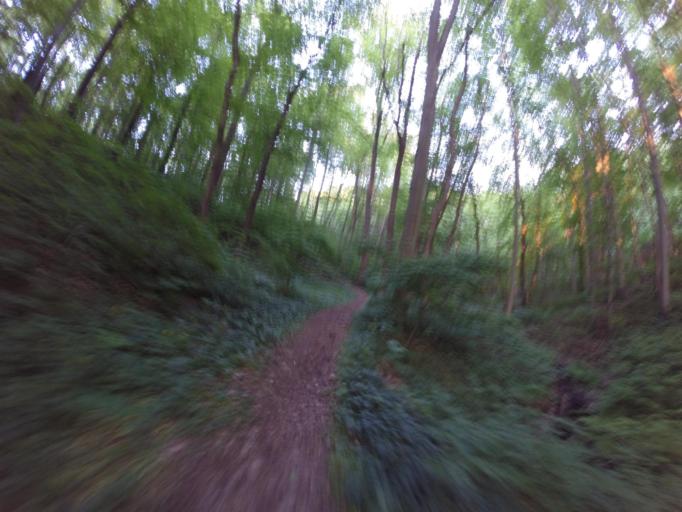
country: DE
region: Thuringia
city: Grosslobichau
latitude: 50.9257
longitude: 11.6557
